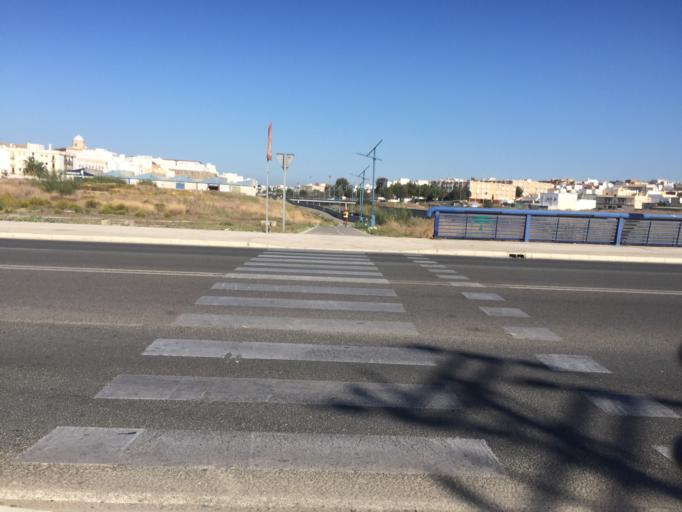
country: ES
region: Andalusia
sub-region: Provincia de Cadiz
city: Chiclana de la Frontera
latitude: 36.4143
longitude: -6.1404
